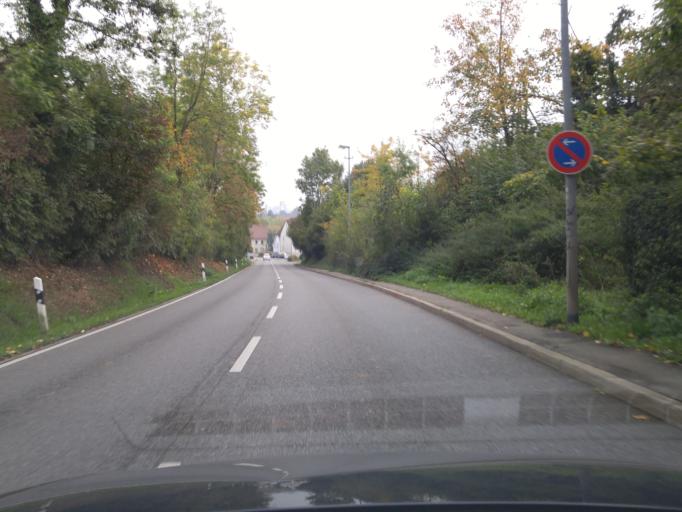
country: DE
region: Baden-Wuerttemberg
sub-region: Regierungsbezirk Stuttgart
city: Heilbronn
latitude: 49.1624
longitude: 9.1709
